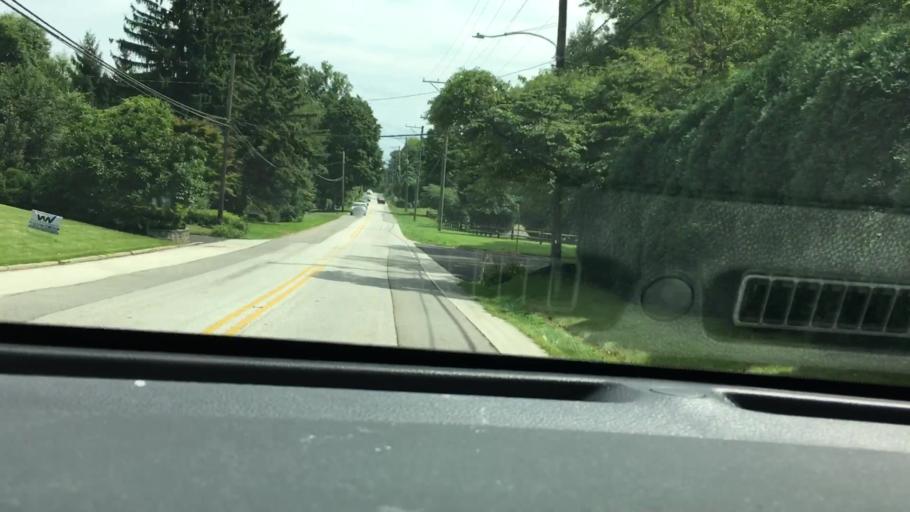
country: US
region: Pennsylvania
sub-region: Montgomery County
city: Bryn Athyn
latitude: 40.1420
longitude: -75.0462
